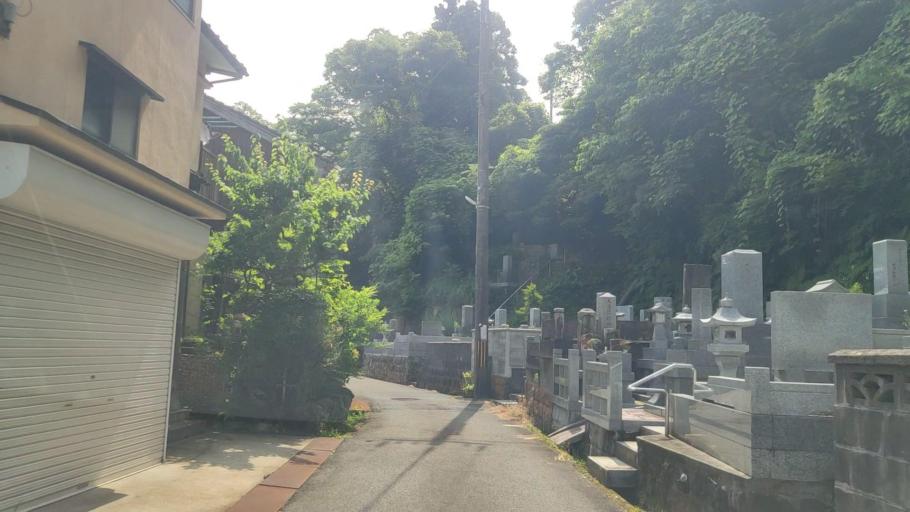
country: JP
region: Hyogo
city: Toyooka
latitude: 35.6244
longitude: 134.8112
